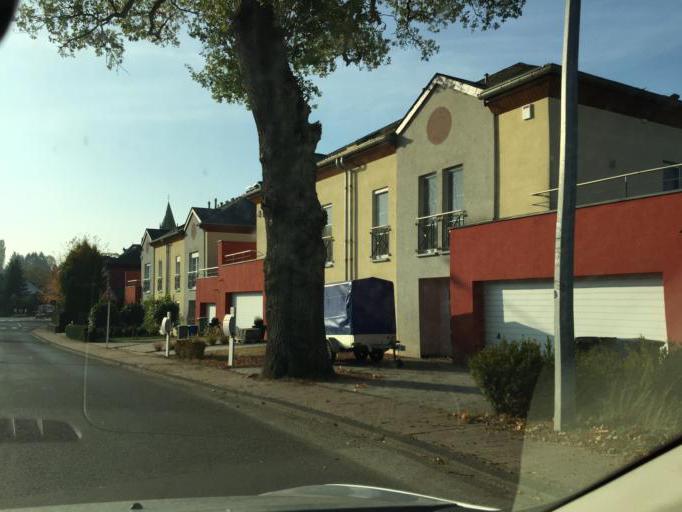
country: LU
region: Luxembourg
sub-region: Canton de Luxembourg
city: Contern
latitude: 49.5663
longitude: 6.2194
